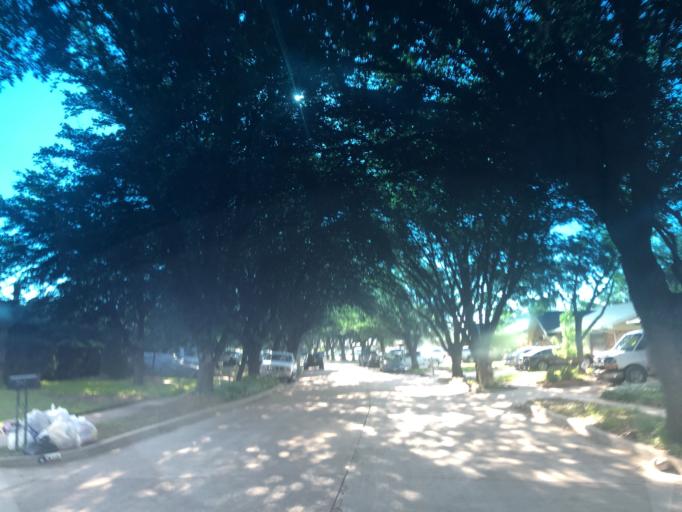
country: US
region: Texas
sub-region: Dallas County
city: Grand Prairie
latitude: 32.7010
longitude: -97.0020
